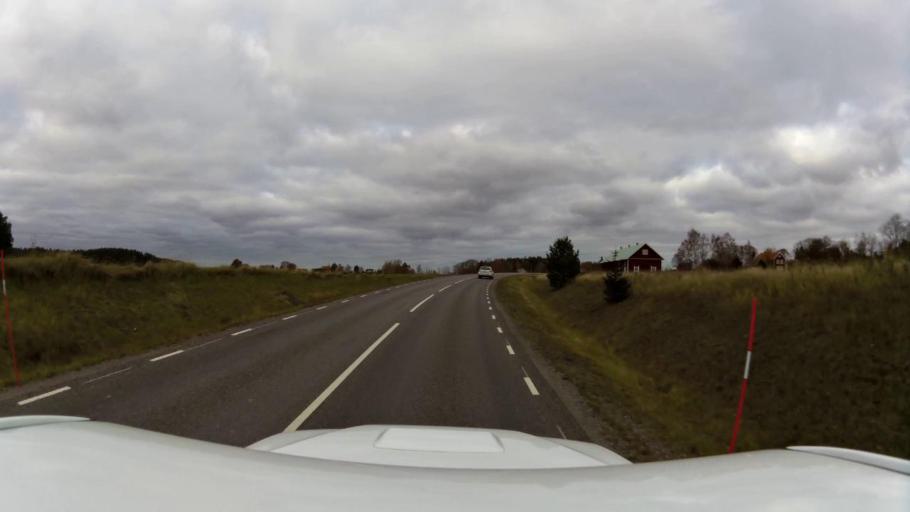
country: SE
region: OEstergoetland
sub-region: Linkopings Kommun
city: Linghem
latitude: 58.4252
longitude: 15.7247
